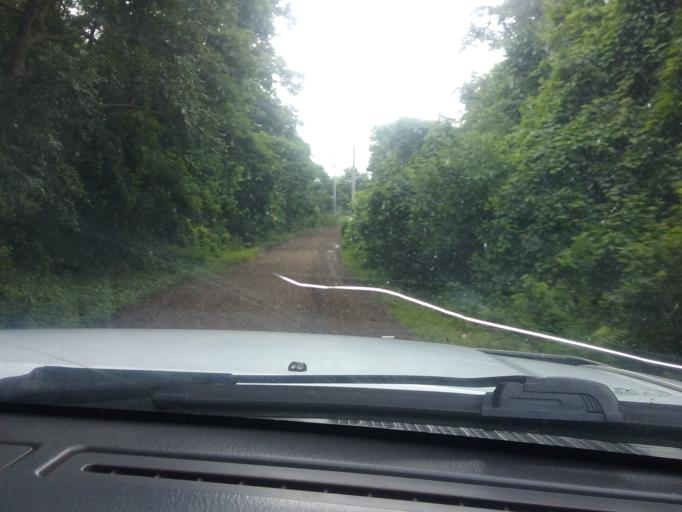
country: NI
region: Matagalpa
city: Matagalpa
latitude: 12.8759
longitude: -85.9593
